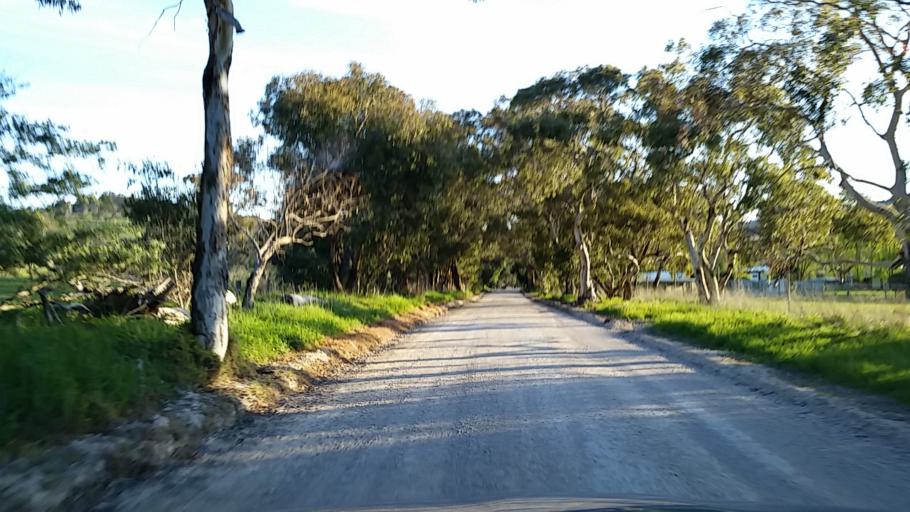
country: AU
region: South Australia
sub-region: Alexandrina
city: Mount Compass
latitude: -35.3183
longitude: 138.6704
